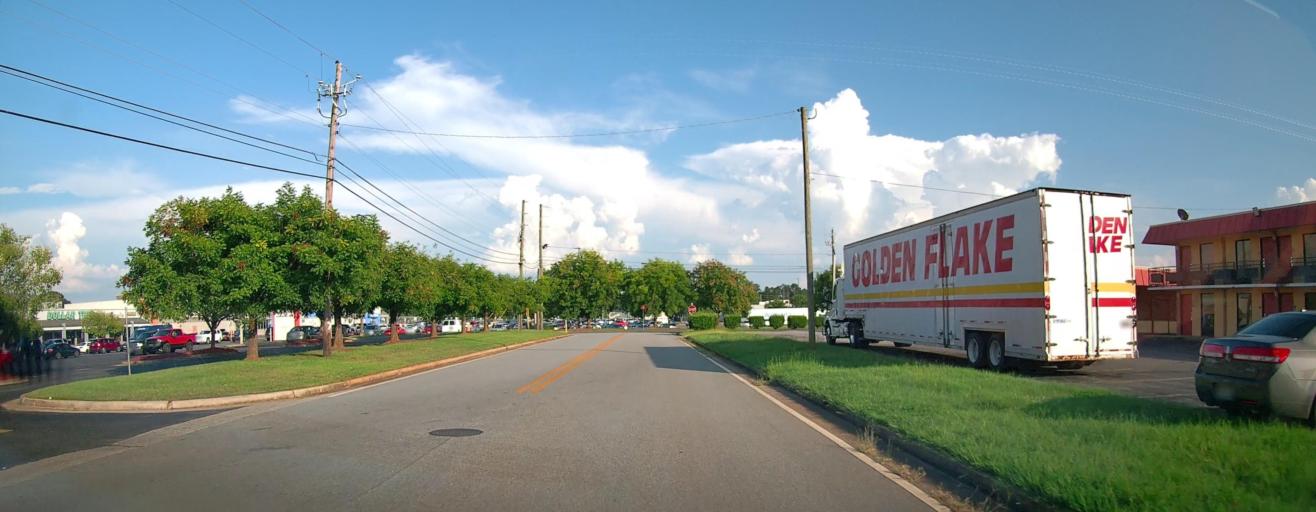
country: US
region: Georgia
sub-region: Houston County
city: Perry
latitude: 32.4730
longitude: -83.7415
